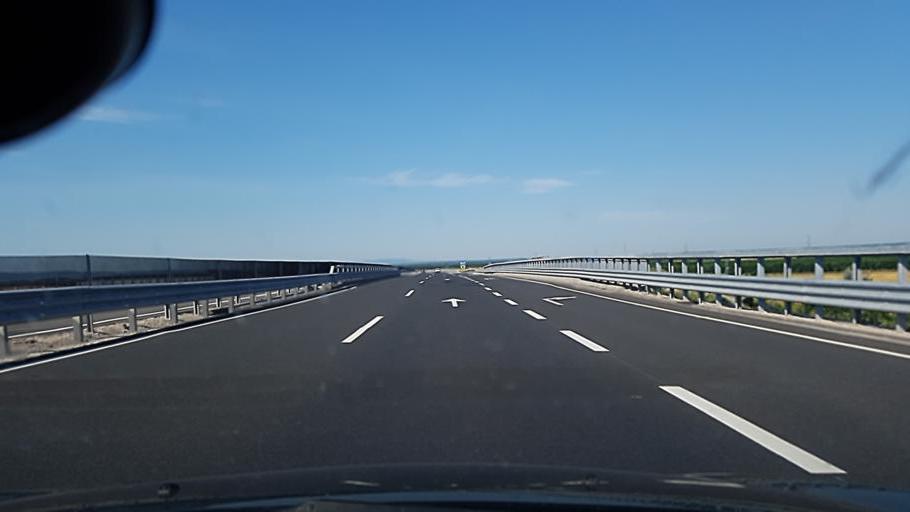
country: HU
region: Tolna
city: Szedres
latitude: 46.4724
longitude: 18.7216
